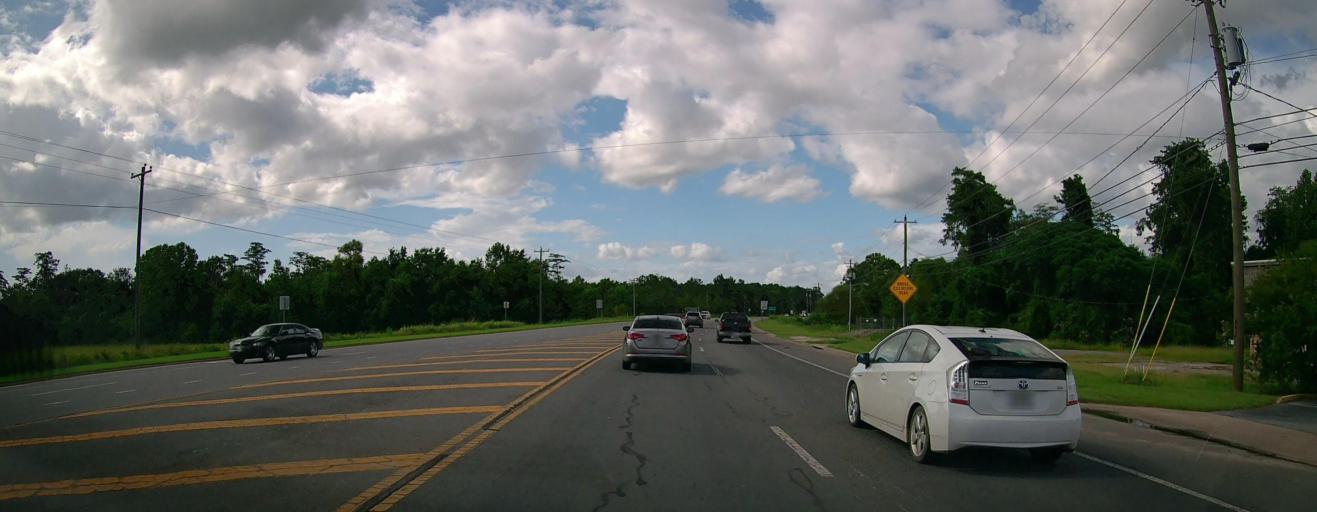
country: US
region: Georgia
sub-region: Coffee County
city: Douglas
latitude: 31.5268
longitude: -82.8505
